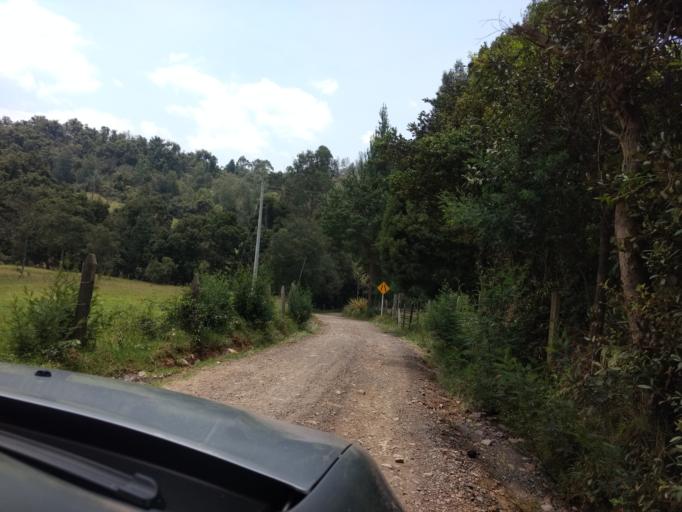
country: CO
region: Boyaca
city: Raquira
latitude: 5.5149
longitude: -73.7080
